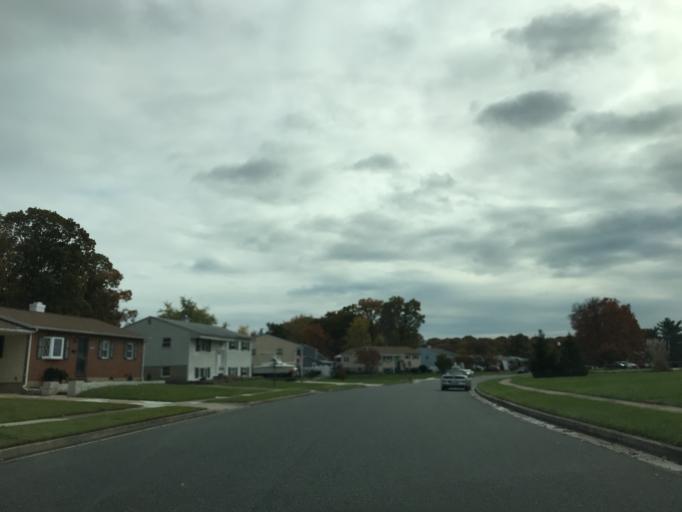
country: US
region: Maryland
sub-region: Baltimore County
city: Bowleys Quarters
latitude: 39.3324
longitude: -76.3914
